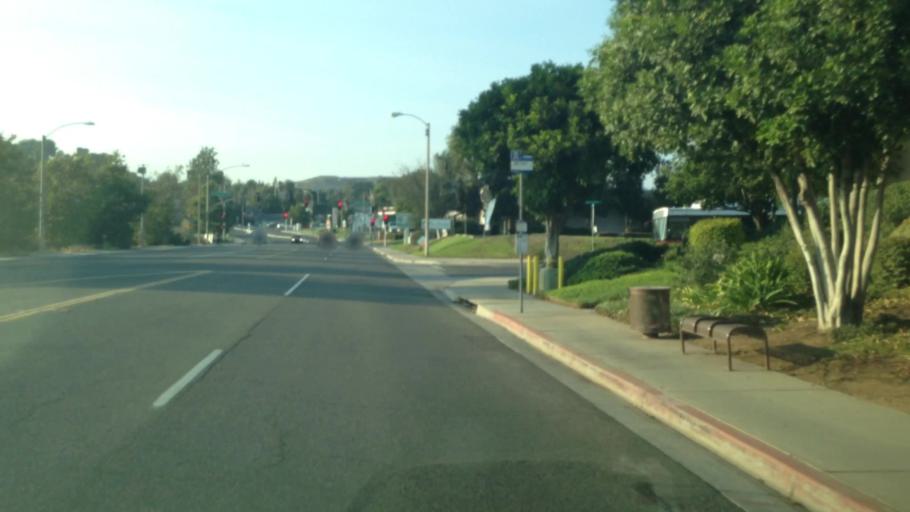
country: US
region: California
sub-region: Riverside County
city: Pedley
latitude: 33.9748
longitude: -117.4622
